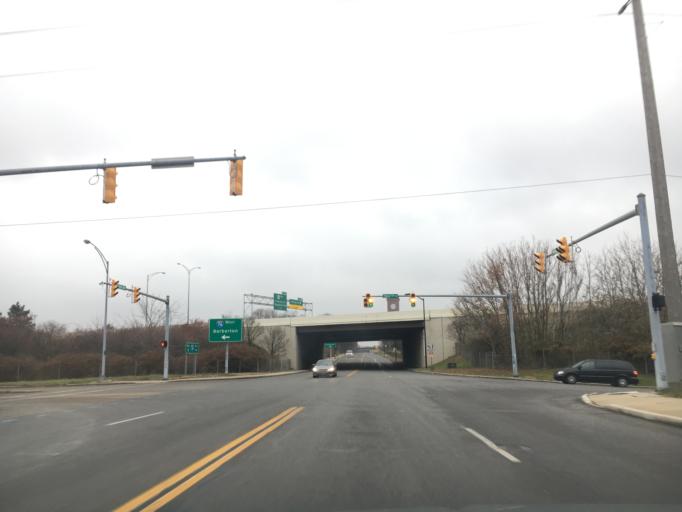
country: US
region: Ohio
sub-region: Summit County
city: Akron
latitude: 41.0633
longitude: -81.4790
